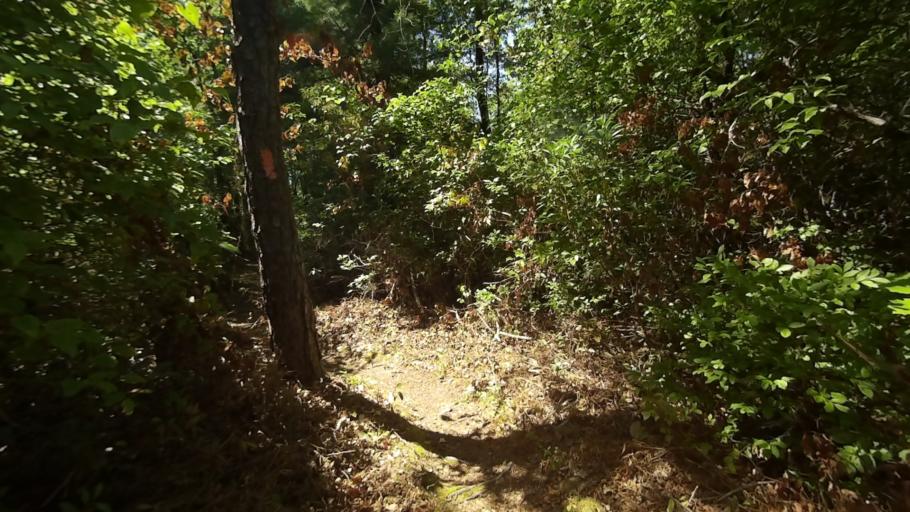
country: US
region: Pennsylvania
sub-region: Centre County
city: Boalsburg
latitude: 40.7260
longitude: -77.7855
